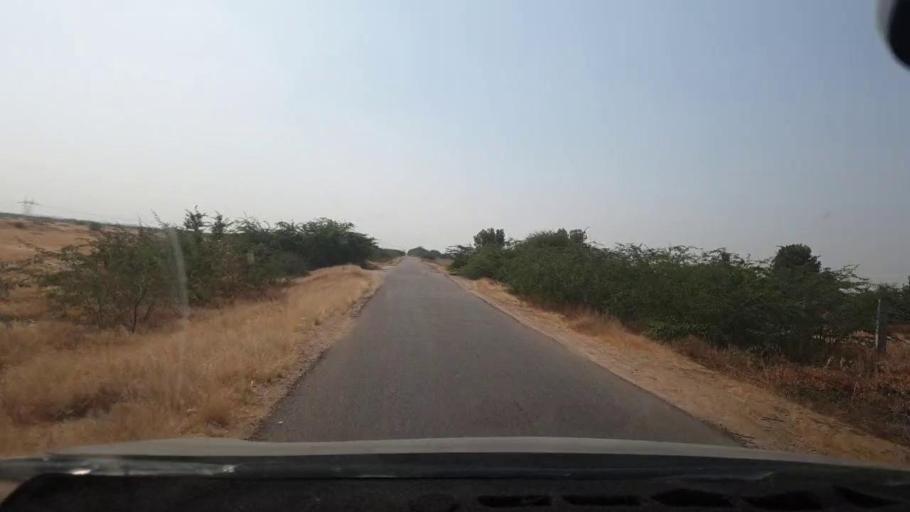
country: PK
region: Sindh
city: Malir Cantonment
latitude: 25.1216
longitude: 67.2180
